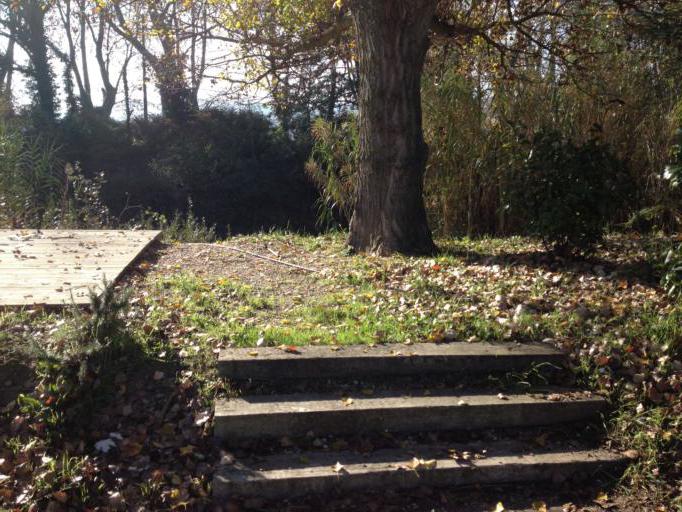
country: FR
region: Provence-Alpes-Cote d'Azur
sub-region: Departement du Vaucluse
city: Bedarrides
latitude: 44.0387
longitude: 4.9031
